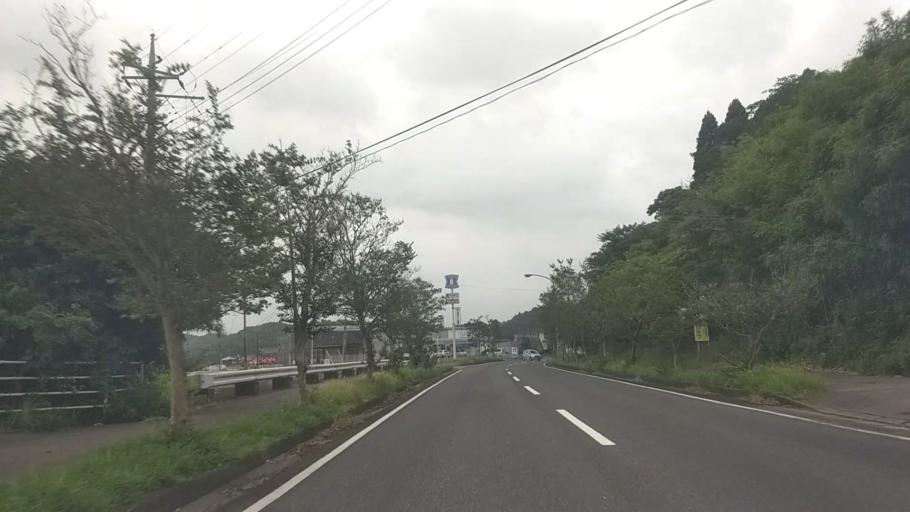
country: JP
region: Chiba
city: Kisarazu
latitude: 35.3772
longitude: 140.0110
